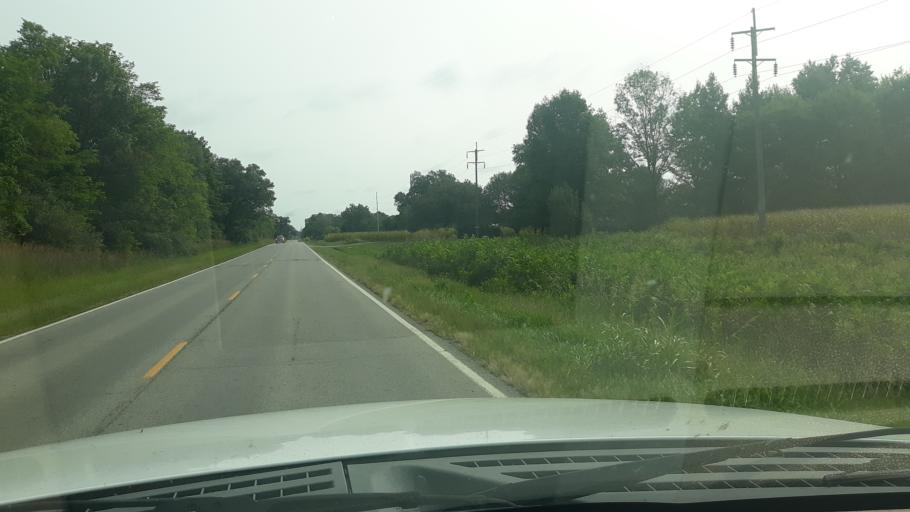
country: US
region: Illinois
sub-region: White County
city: Norris City
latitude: 37.8946
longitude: -88.3775
